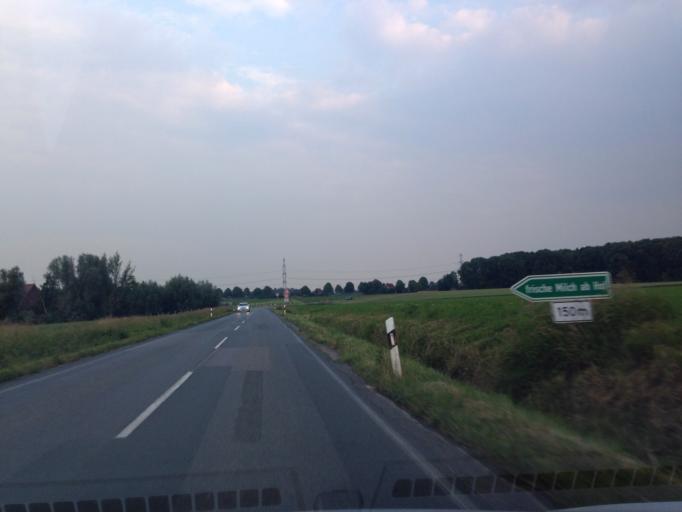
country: DE
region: North Rhine-Westphalia
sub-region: Regierungsbezirk Munster
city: Altenberge
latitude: 51.9714
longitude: 7.5261
